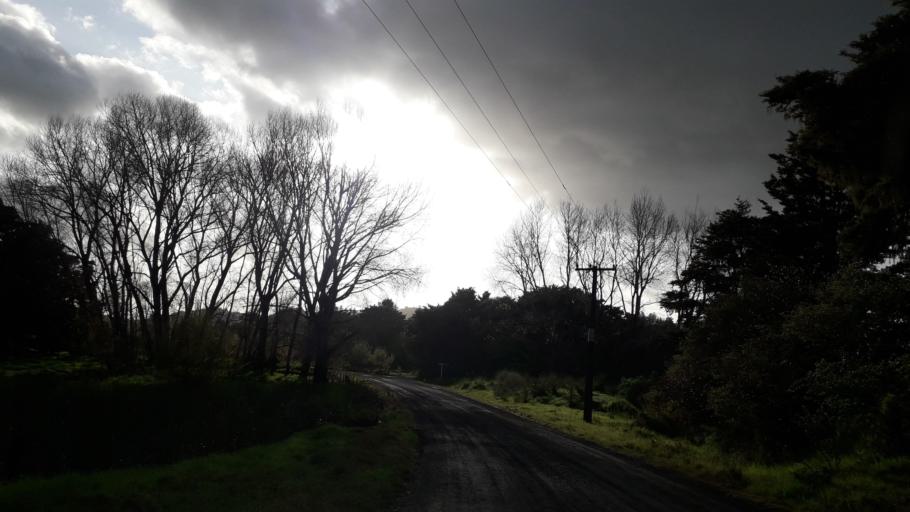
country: NZ
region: Northland
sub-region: Far North District
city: Waimate North
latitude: -35.5040
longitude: 173.7017
